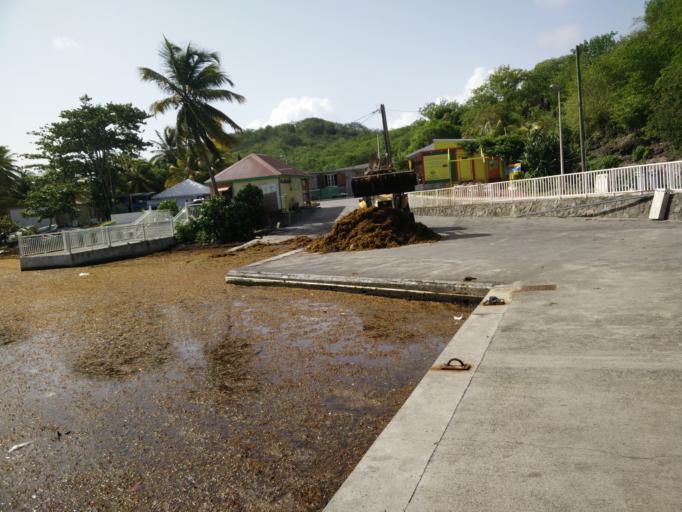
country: GP
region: Guadeloupe
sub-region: Guadeloupe
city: Terre-de-Bas
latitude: 15.8545
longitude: -61.6159
